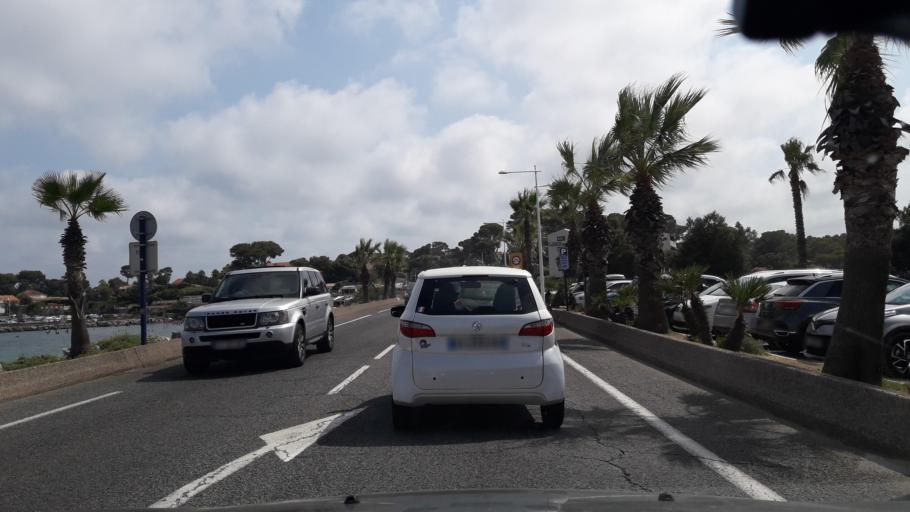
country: FR
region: Provence-Alpes-Cote d'Azur
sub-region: Departement du Var
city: Frejus
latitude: 43.3943
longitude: 6.7283
